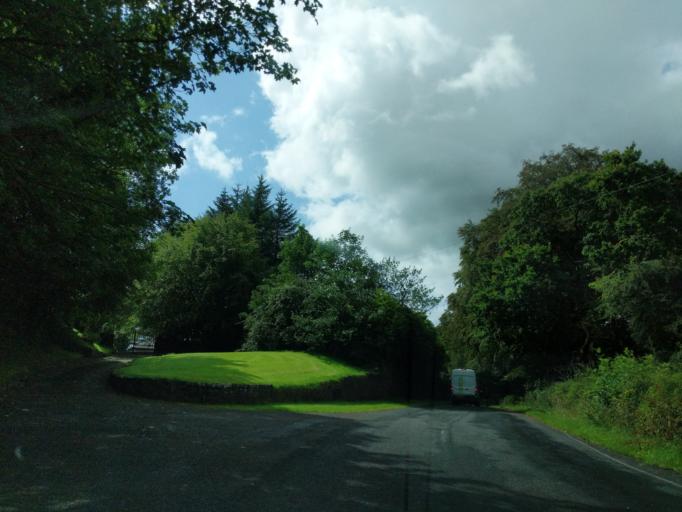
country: GB
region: Scotland
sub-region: East Ayrshire
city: Stewarton
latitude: 55.7143
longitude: -4.5221
